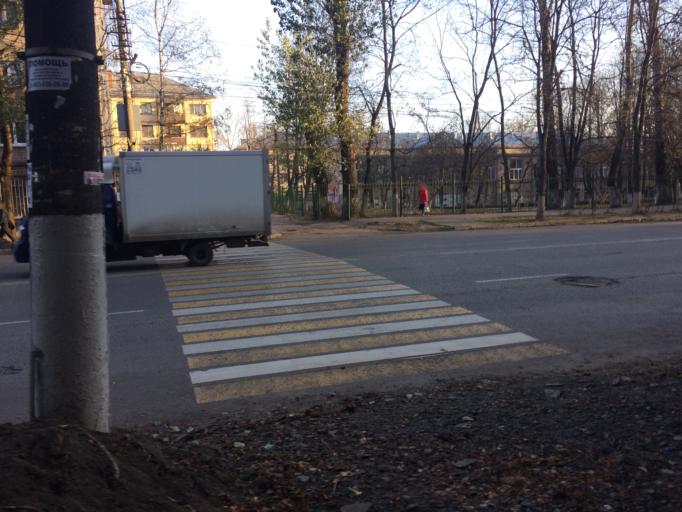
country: RU
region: Tula
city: Mendeleyevskiy
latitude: 54.1638
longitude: 37.5933
